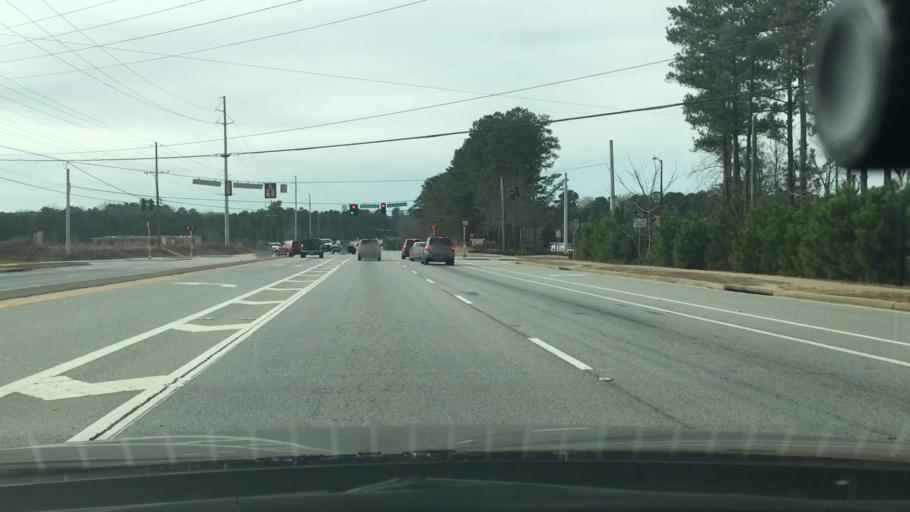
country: US
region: Georgia
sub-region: Coweta County
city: Senoia
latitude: 33.3422
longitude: -84.5327
